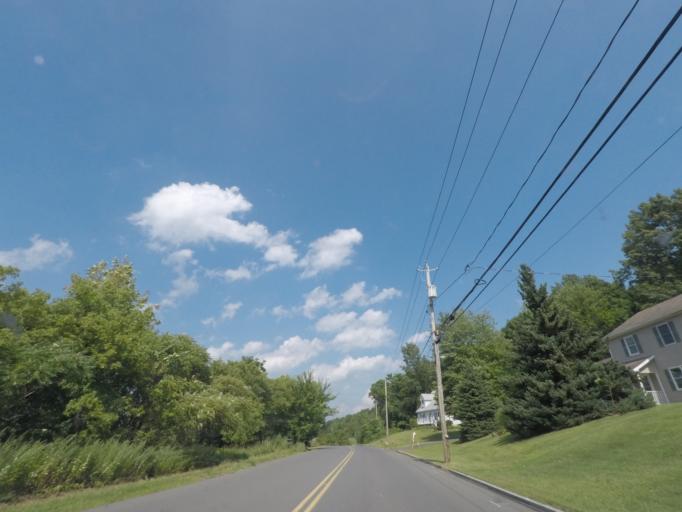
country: US
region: New York
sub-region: Saratoga County
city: Waterford
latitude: 42.7796
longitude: -73.6634
